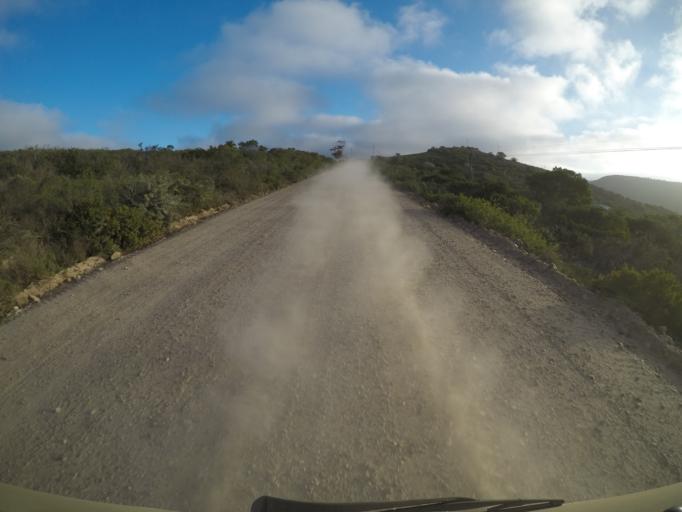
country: ZA
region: Western Cape
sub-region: Eden District Municipality
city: Mossel Bay
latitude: -34.1288
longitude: 22.0480
